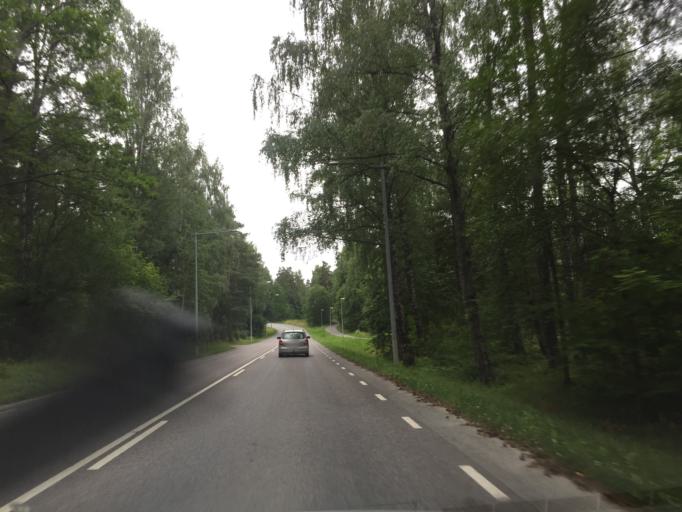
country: SE
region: OErebro
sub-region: Orebro Kommun
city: Orebro
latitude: 59.2478
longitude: 15.1988
